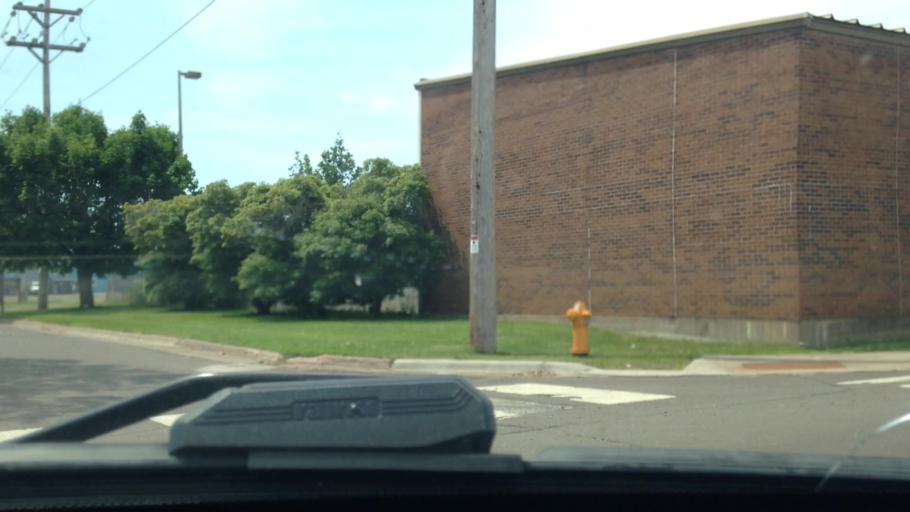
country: US
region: Wisconsin
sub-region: Douglas County
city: Superior
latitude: 46.7352
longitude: -92.1009
